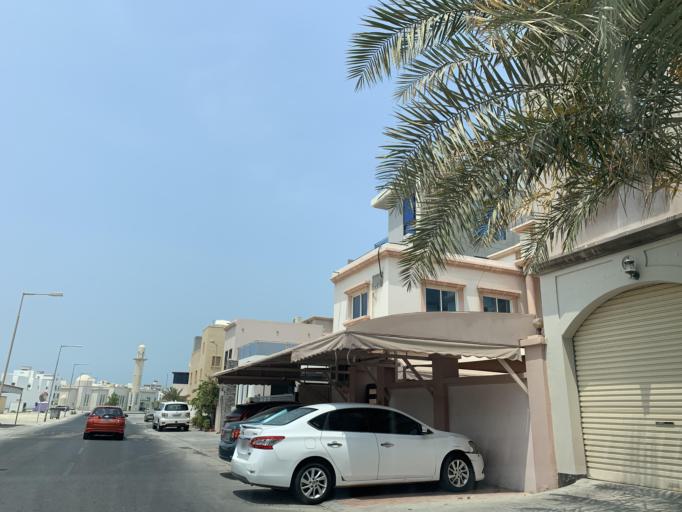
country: BH
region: Muharraq
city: Al Hadd
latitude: 26.2777
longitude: 50.6449
